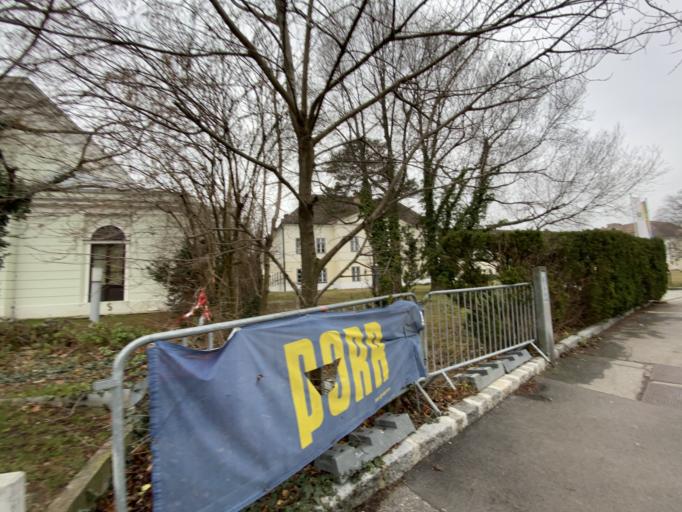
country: AT
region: Lower Austria
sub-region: Politischer Bezirk Baden
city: Baden
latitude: 48.0060
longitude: 16.2300
